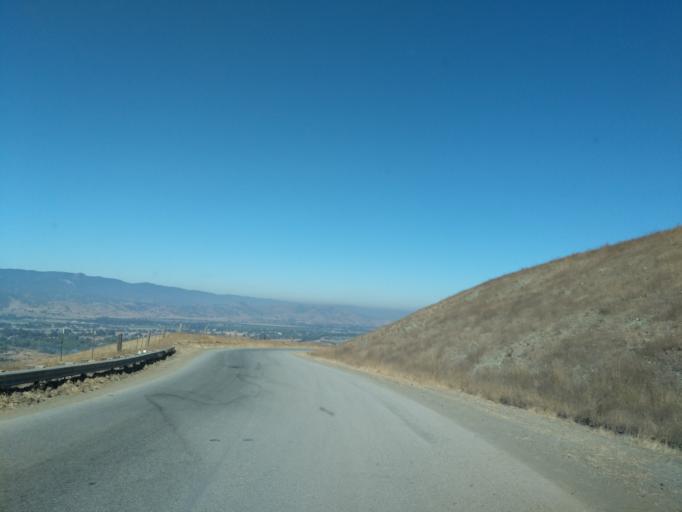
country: US
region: California
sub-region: Santa Clara County
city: Morgan Hill
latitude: 37.1819
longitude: -121.6705
